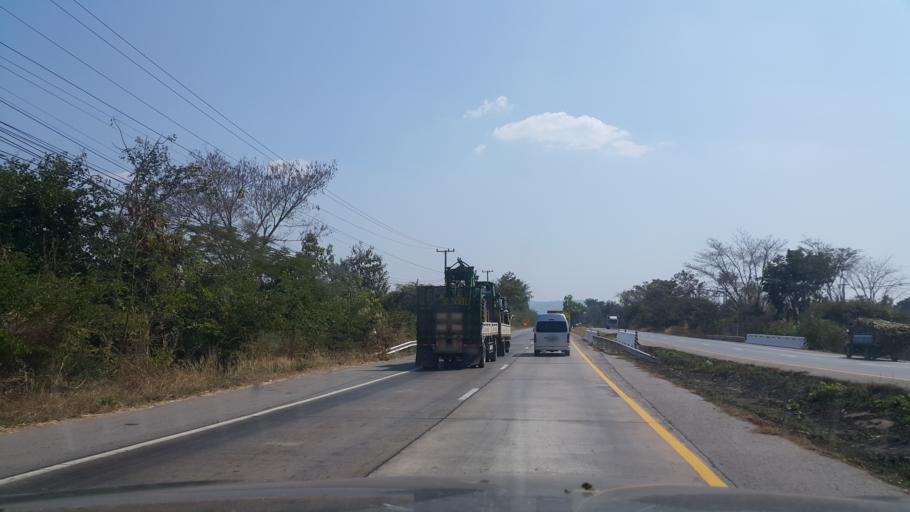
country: TH
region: Changwat Udon Thani
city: Non Sa-at
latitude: 16.8954
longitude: 102.8746
